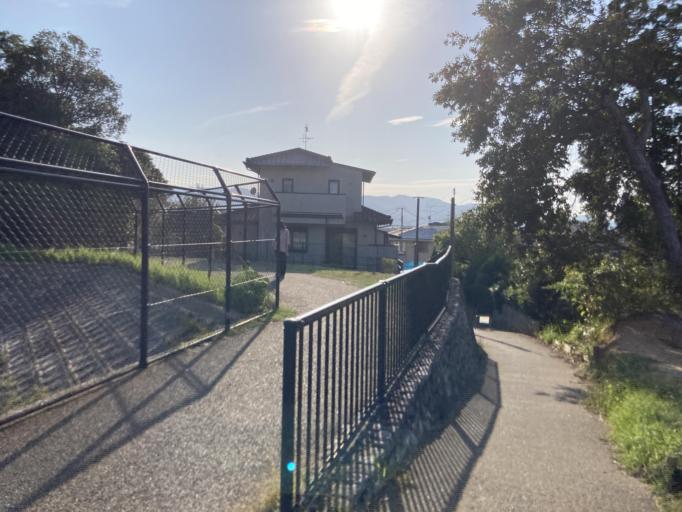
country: JP
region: Fukuoka
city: Fukuoka-shi
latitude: 33.5497
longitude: 130.3526
